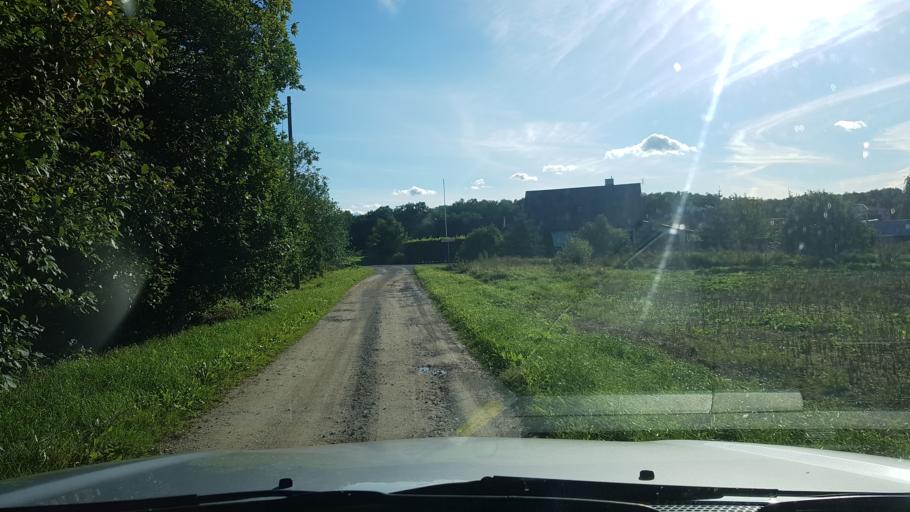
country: EE
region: Harju
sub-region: Rae vald
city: Jueri
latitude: 59.3848
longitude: 24.8709
